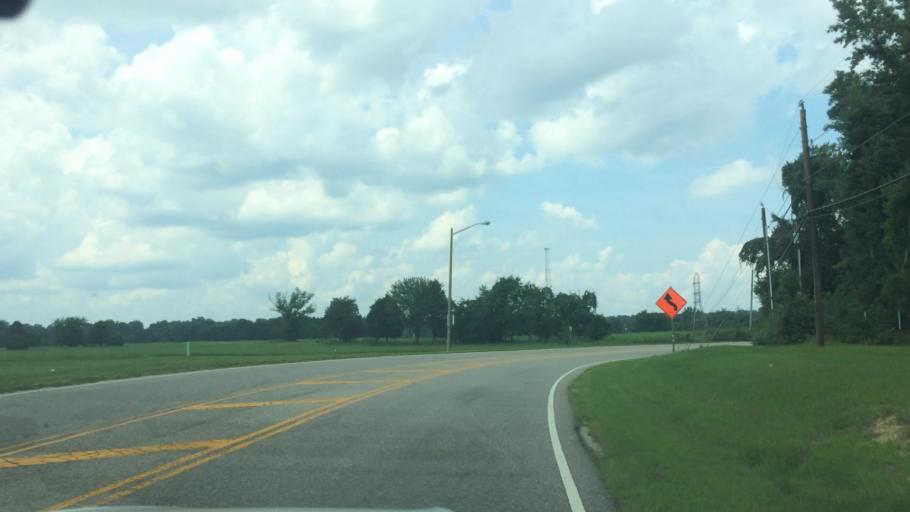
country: US
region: Virginia
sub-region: York County
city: Yorktown
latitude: 37.2020
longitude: -76.5749
